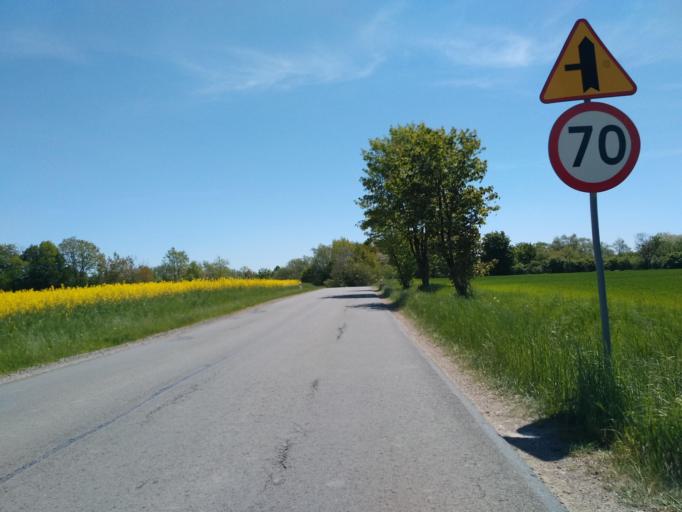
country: PL
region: Subcarpathian Voivodeship
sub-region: Powiat krosnienski
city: Sieniawa
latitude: 49.5455
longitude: 21.9487
